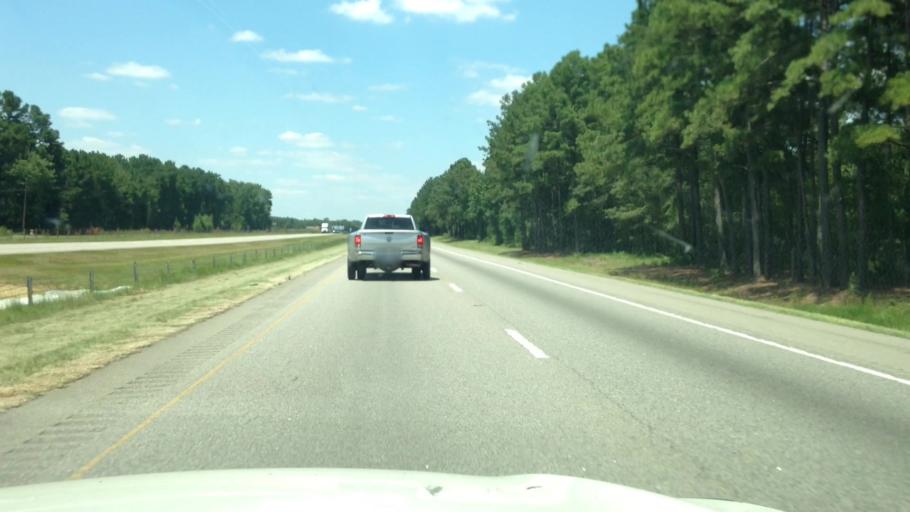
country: US
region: North Carolina
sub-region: Robeson County
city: Saint Pauls
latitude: 34.7841
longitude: -78.9949
